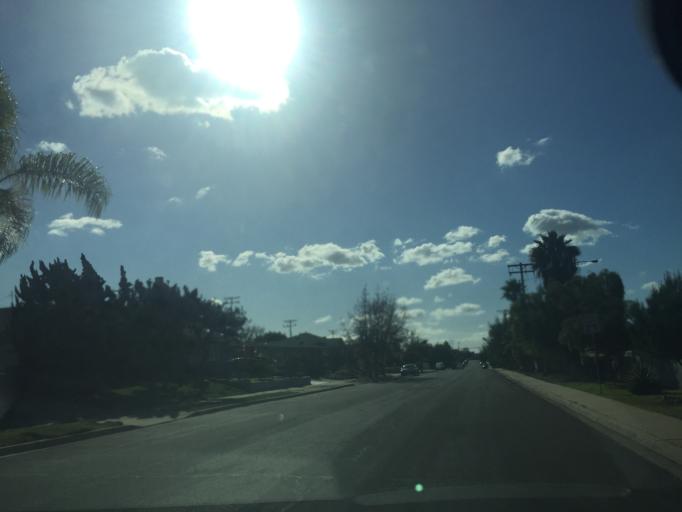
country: US
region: California
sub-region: San Diego County
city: La Mesa
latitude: 32.7917
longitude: -117.0795
